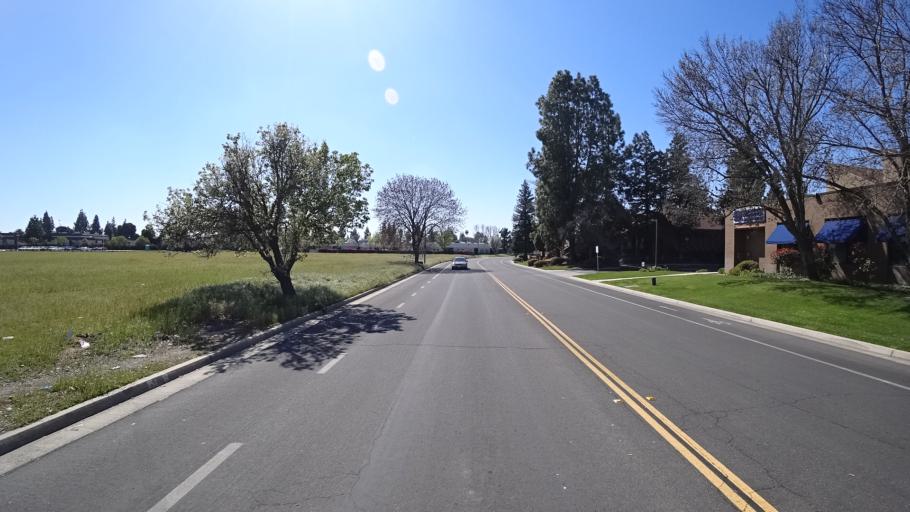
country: US
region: California
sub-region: Fresno County
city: Tarpey Village
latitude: 36.7720
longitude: -119.7269
